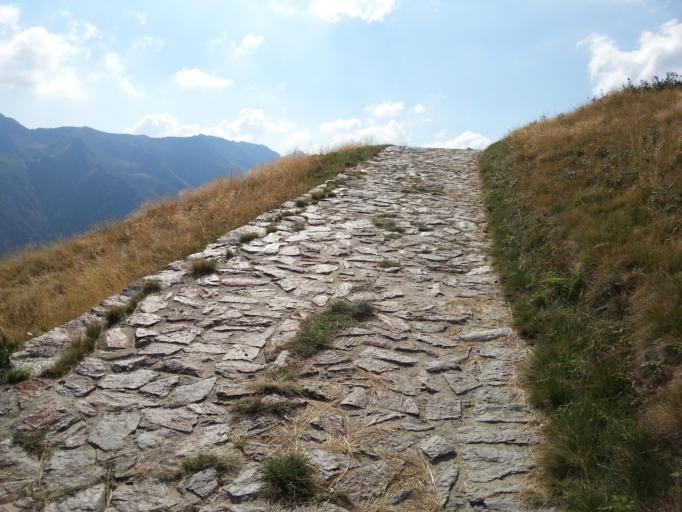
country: IT
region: Lombardy
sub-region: Provincia di Como
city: San Bartolomeo Val Cavargna
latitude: 46.1556
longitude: 9.1704
